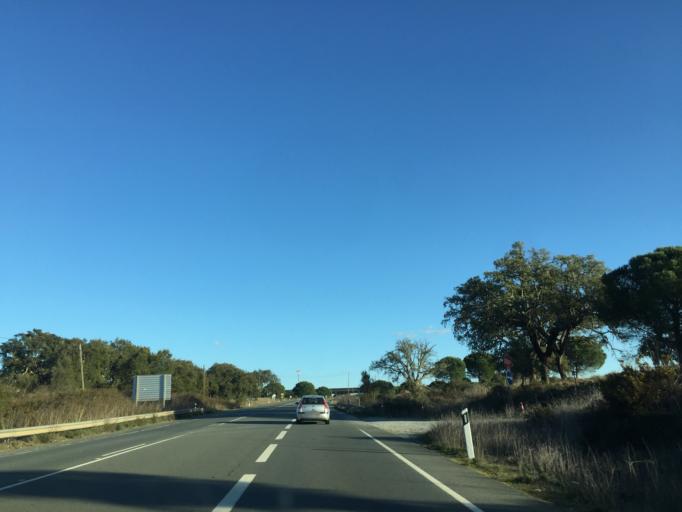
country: PT
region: Setubal
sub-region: Grandola
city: Grandola
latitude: 38.1193
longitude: -8.4244
